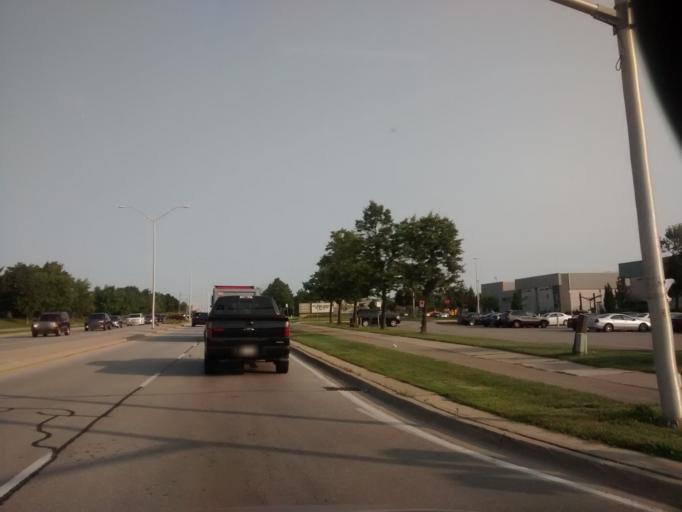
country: CA
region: Ontario
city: Oakville
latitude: 43.4346
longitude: -79.7387
